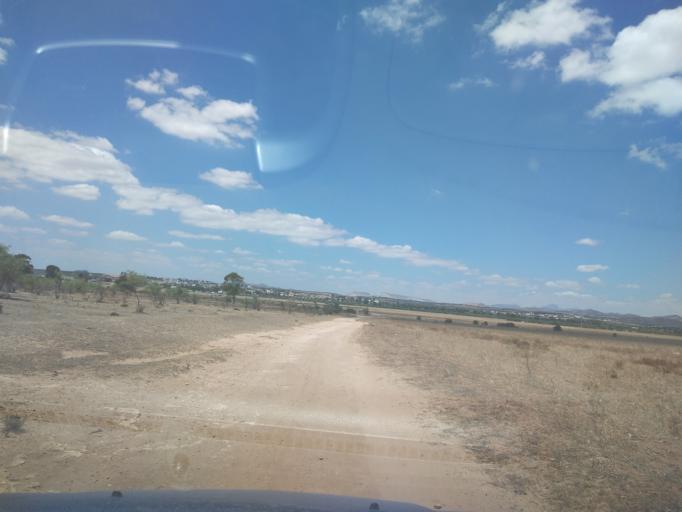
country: TN
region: Susah
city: Harqalah
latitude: 36.1679
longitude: 10.4362
